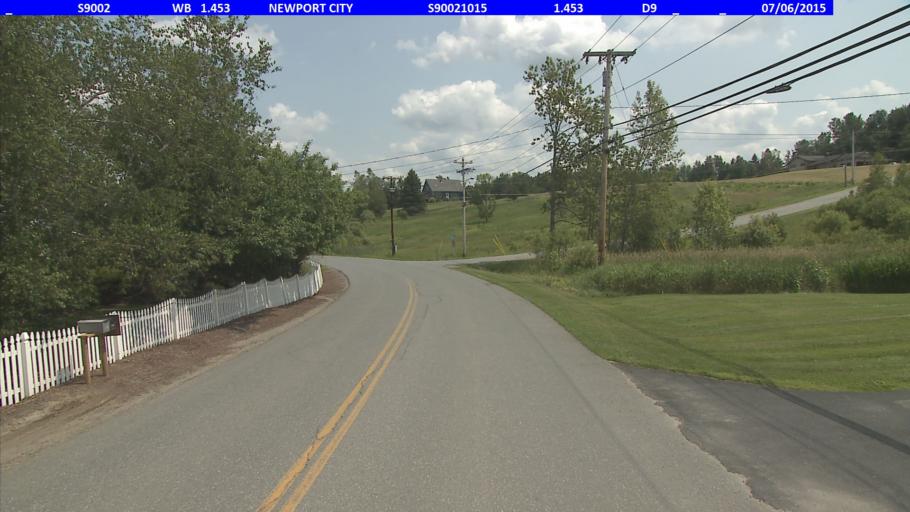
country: US
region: Vermont
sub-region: Orleans County
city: Newport
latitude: 44.9368
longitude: -72.2348
